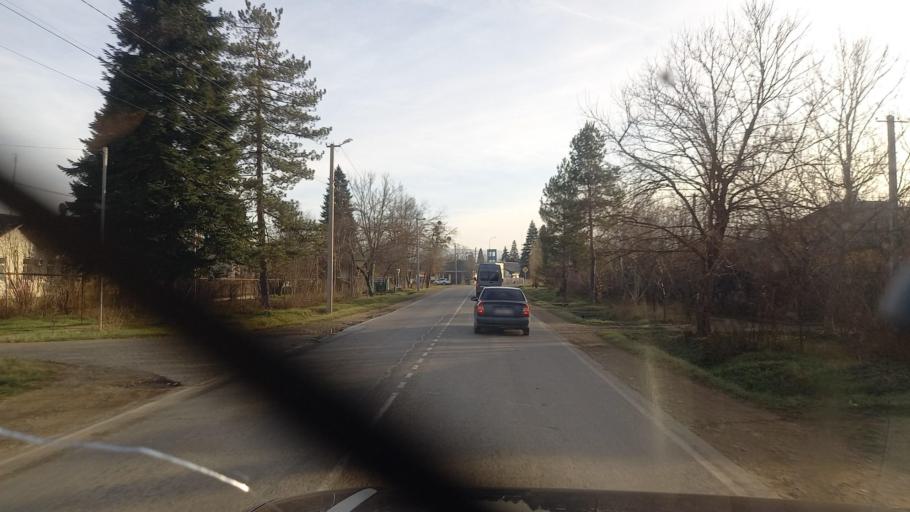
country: RU
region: Krasnodarskiy
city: Khadyzhensk
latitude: 44.4386
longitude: 39.5263
